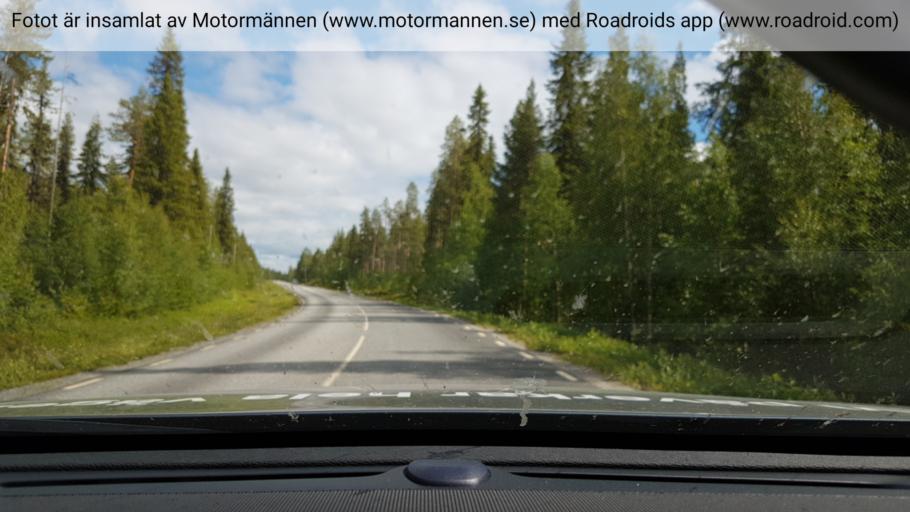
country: SE
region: Vaesterbotten
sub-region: Sorsele Kommun
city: Sorsele
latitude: 65.6920
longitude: 17.1831
